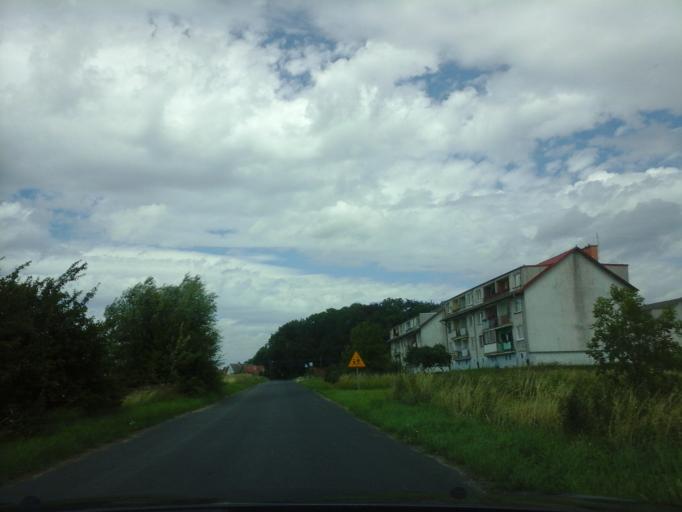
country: PL
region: West Pomeranian Voivodeship
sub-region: Powiat choszczenski
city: Recz
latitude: 53.2865
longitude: 15.4952
